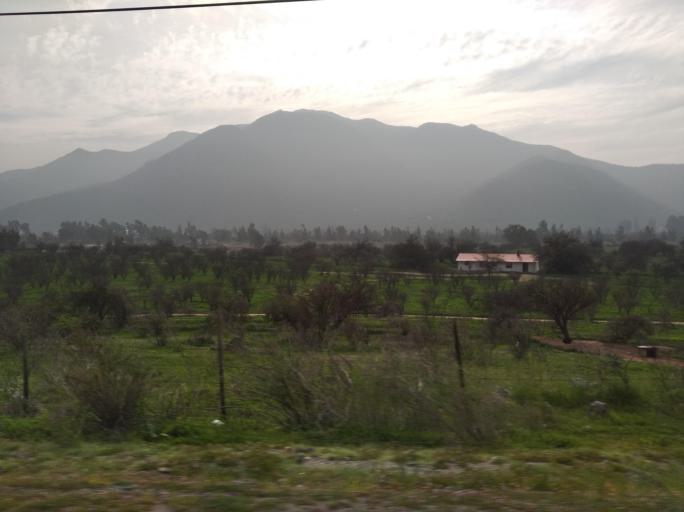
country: CL
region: Santiago Metropolitan
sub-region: Provincia de Chacabuco
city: Lampa
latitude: -33.2566
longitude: -70.9037
